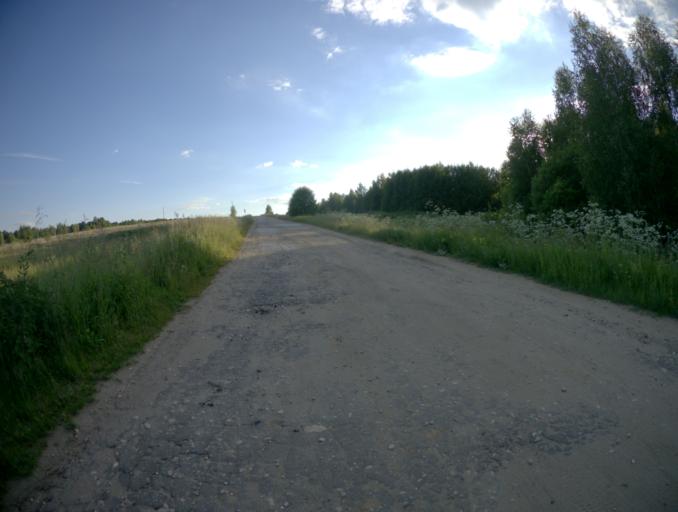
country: RU
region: Vladimir
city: Stavrovo
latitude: 56.2903
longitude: 39.9962
